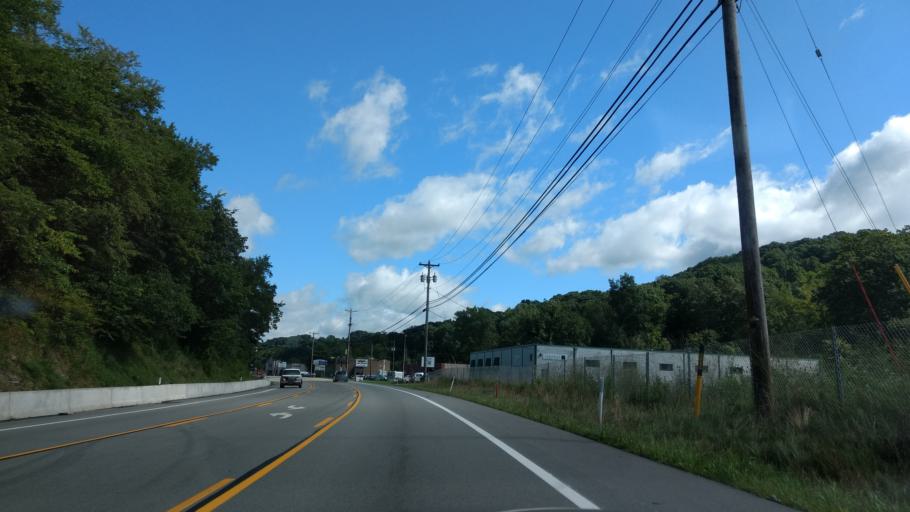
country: US
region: Pennsylvania
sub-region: Westmoreland County
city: Murrysville
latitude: 40.4369
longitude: -79.7130
